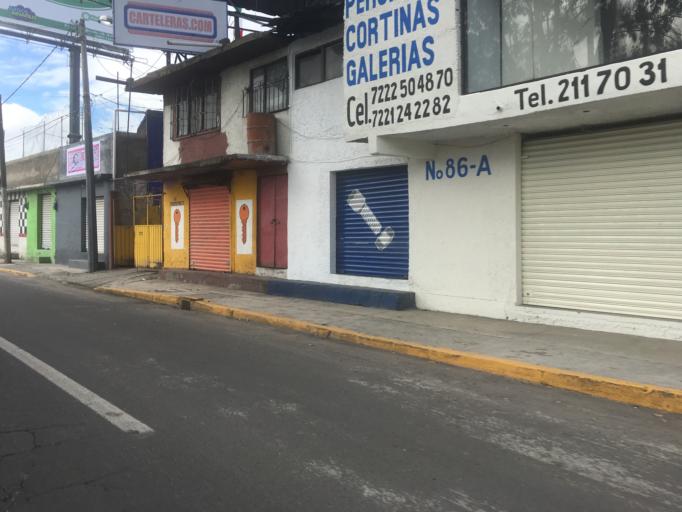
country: MX
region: Morelos
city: Metepec
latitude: 19.2836
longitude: -99.6098
